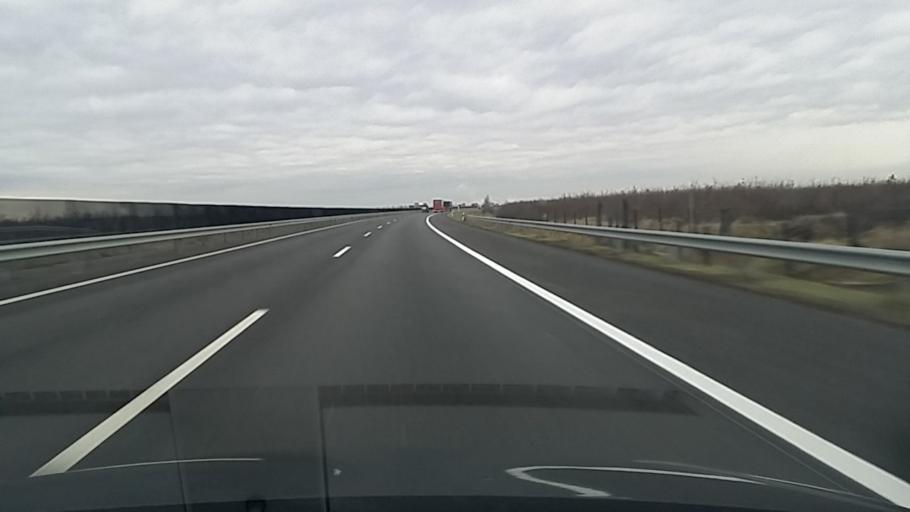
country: HU
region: Hajdu-Bihar
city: Polgar
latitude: 47.8099
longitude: 21.1621
